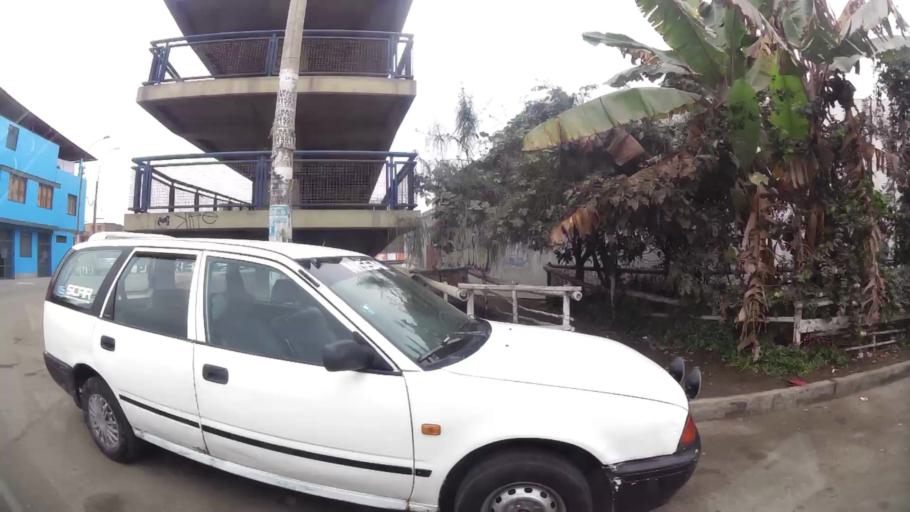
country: PE
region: Lima
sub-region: Lima
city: Surco
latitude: -12.1632
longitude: -76.9552
